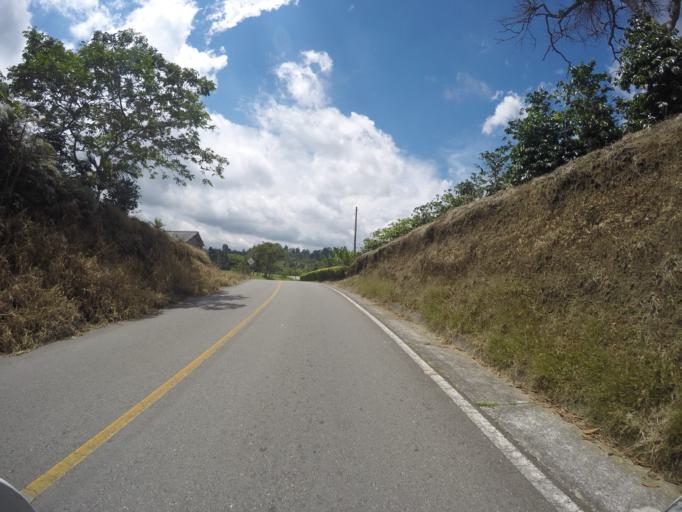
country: CO
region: Quindio
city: Filandia
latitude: 4.6360
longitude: -75.6986
